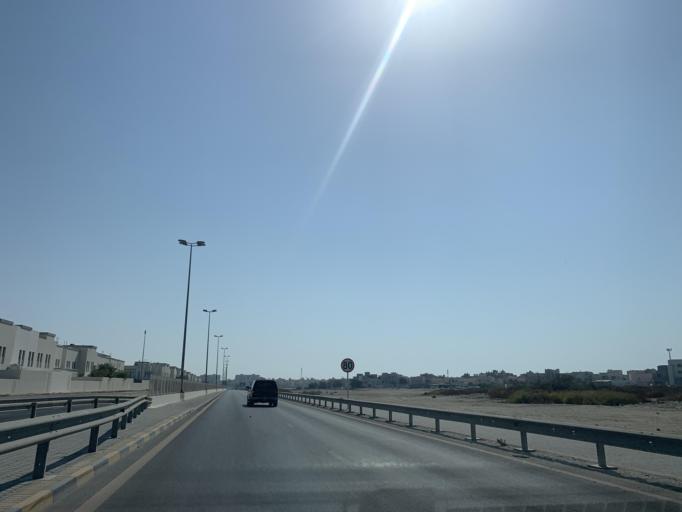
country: BH
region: Central Governorate
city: Madinat Hamad
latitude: 26.1331
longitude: 50.4820
